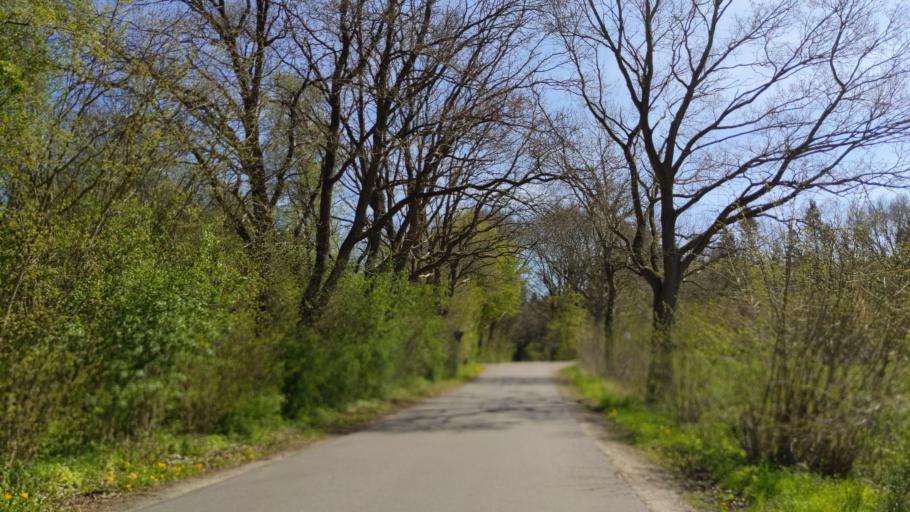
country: DE
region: Schleswig-Holstein
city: Ratekau
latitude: 53.9255
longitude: 10.7686
